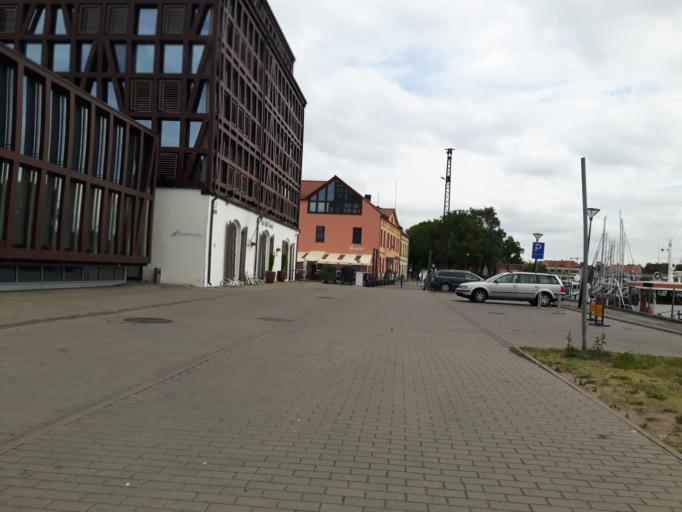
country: LT
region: Klaipedos apskritis
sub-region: Klaipeda
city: Klaipeda
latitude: 55.7065
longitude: 21.1263
